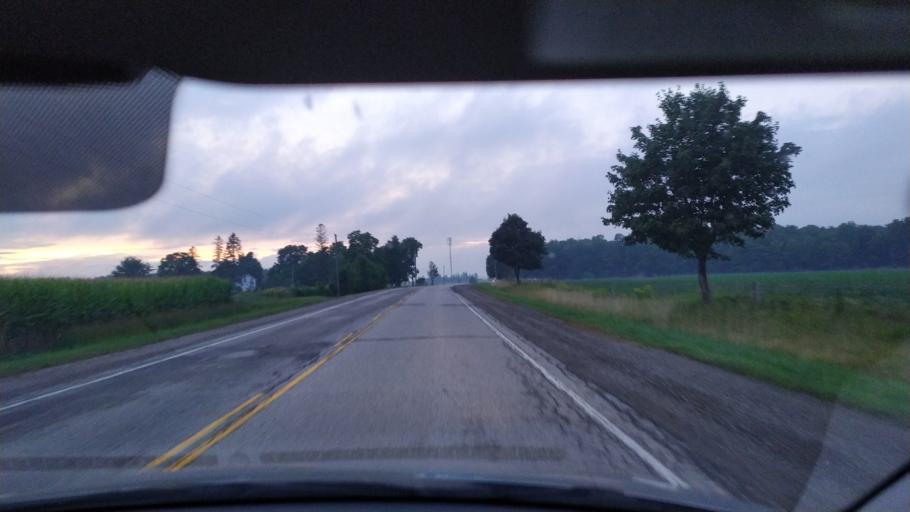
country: CA
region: Ontario
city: Kitchener
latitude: 43.3564
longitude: -80.7023
